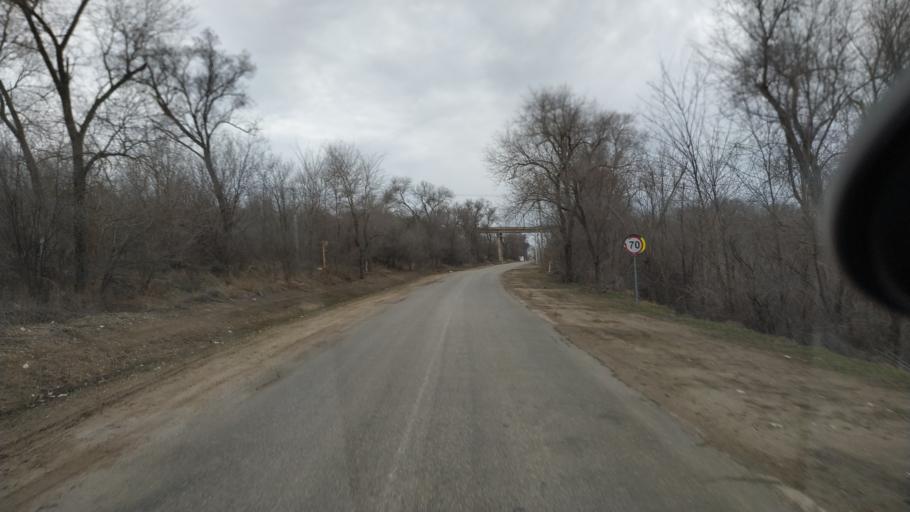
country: MD
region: Criuleni
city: Criuleni
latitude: 47.2328
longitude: 29.1570
